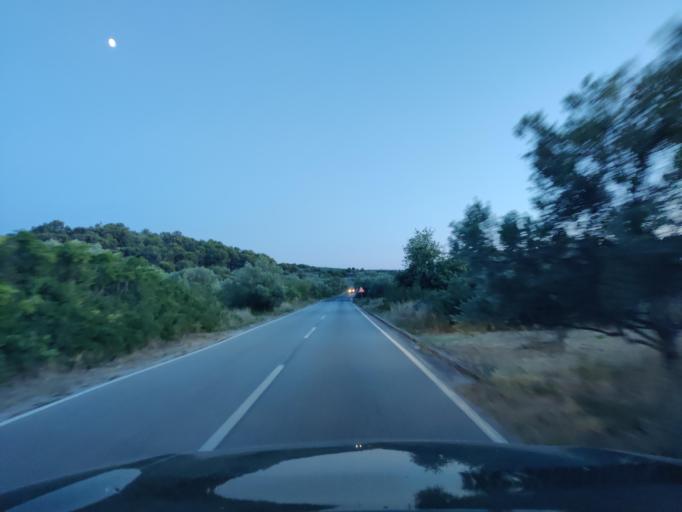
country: HR
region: Sibensko-Kniniska
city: Murter
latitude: 43.8190
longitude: 15.6013
